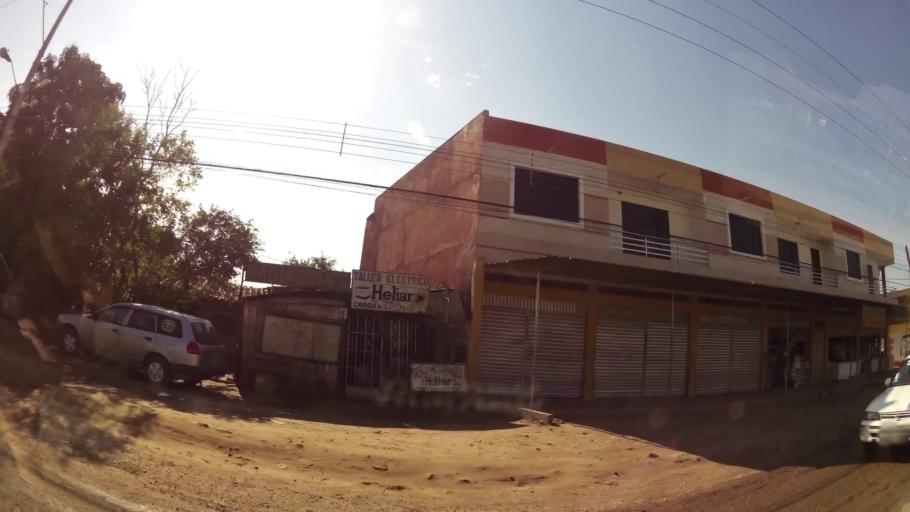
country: BO
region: Santa Cruz
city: Santa Cruz de la Sierra
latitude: -17.8274
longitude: -63.1366
